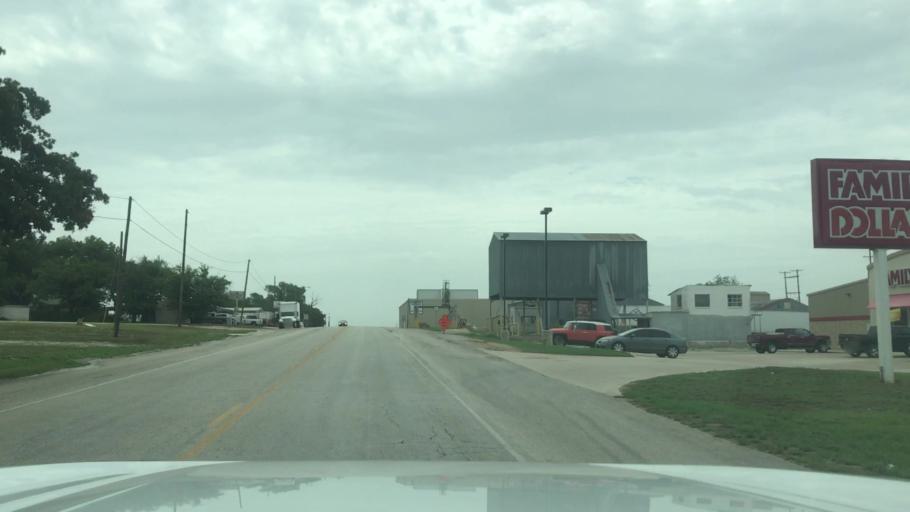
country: US
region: Texas
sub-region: Eastland County
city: Gorman
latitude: 32.2111
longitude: -98.6674
